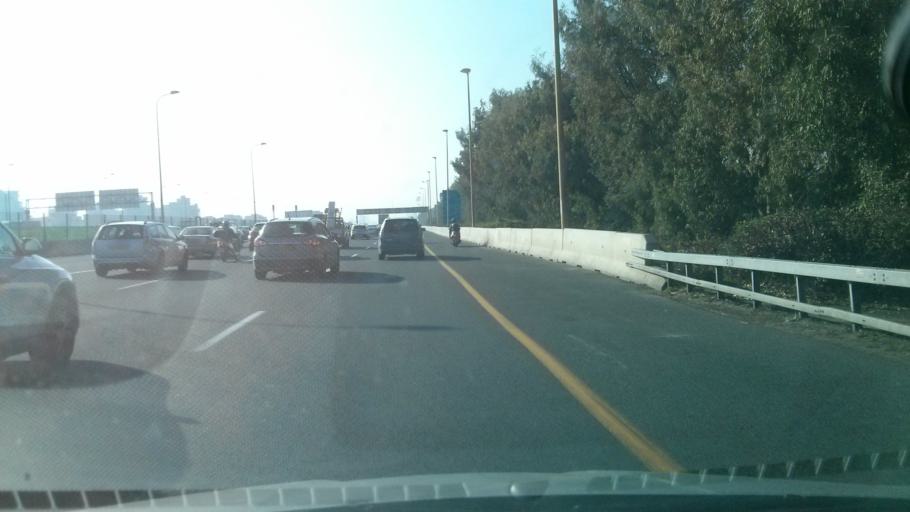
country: IL
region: Tel Aviv
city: Ramat HaSharon
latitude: 32.1339
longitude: 34.8095
